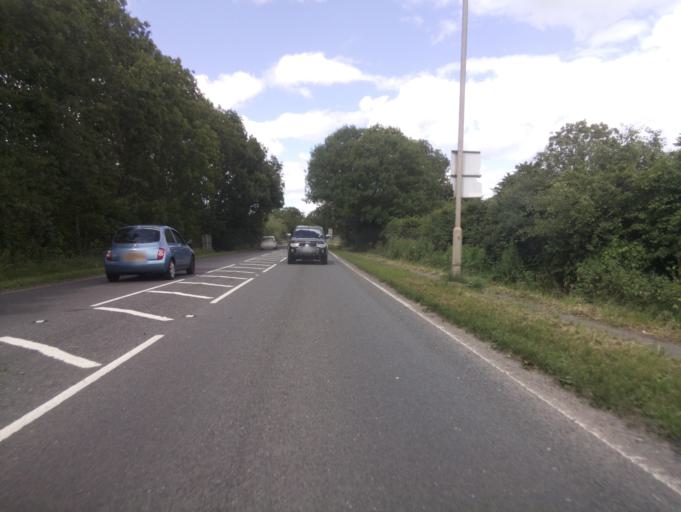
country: GB
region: England
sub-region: Nottinghamshire
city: East Leake
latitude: 52.8334
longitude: -1.1460
